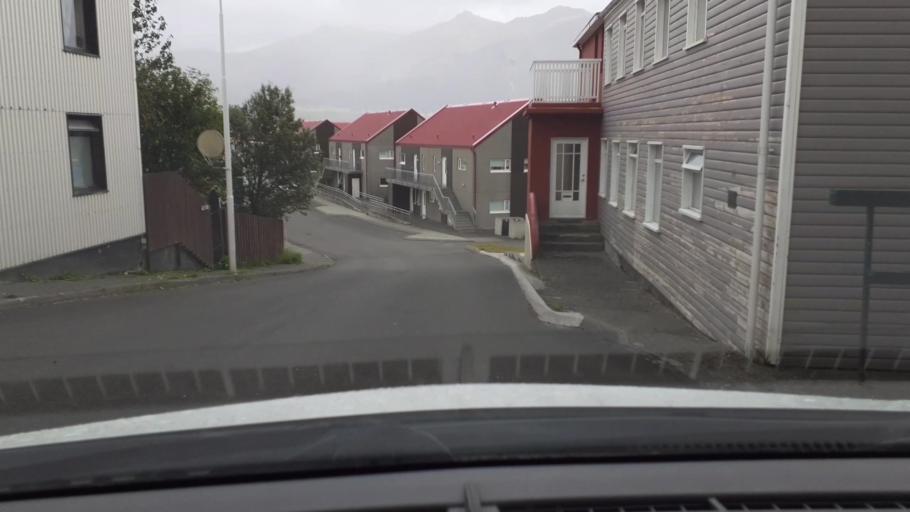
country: IS
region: West
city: Borgarnes
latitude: 64.5371
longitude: -21.9254
